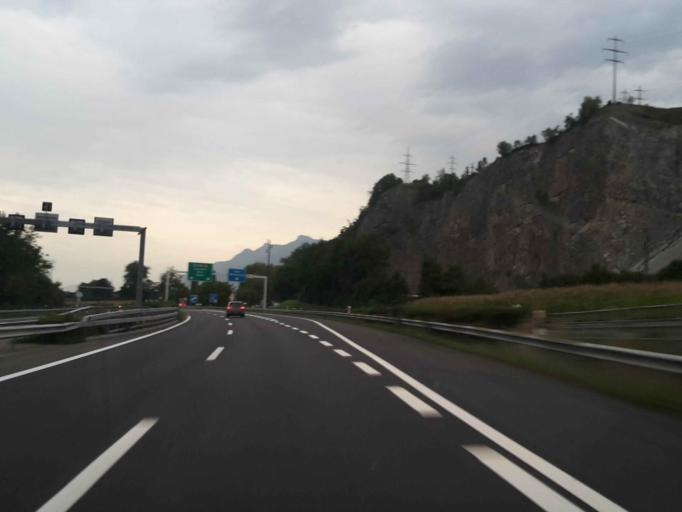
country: CH
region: Valais
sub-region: Saint-Maurice District
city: Saint-Maurice
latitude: 46.2317
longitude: 7.0036
